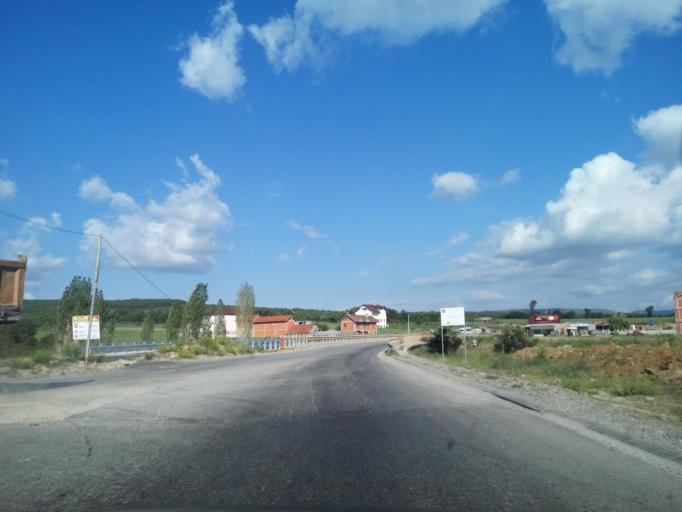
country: XK
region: Prizren
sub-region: Komuna e Malisheves
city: Llazice
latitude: 42.5647
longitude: 20.7699
